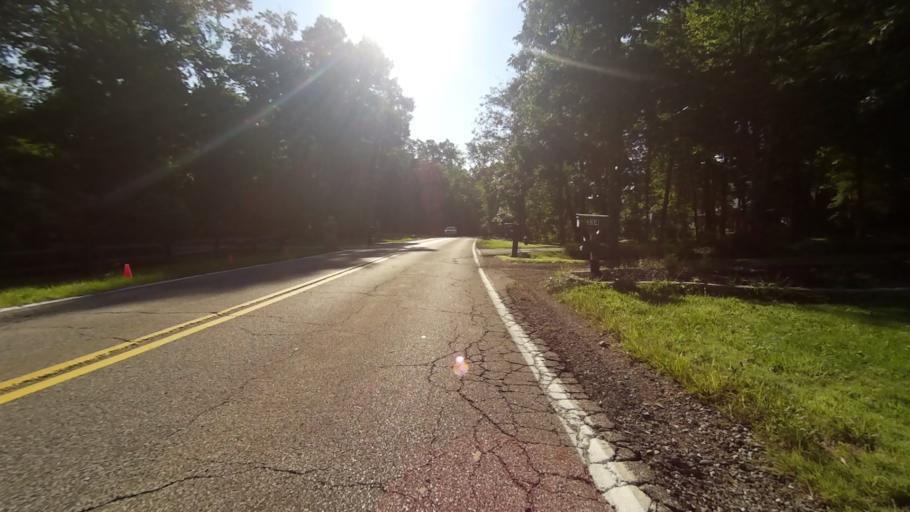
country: US
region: Ohio
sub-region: Portage County
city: Aurora
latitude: 41.3097
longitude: -81.3348
